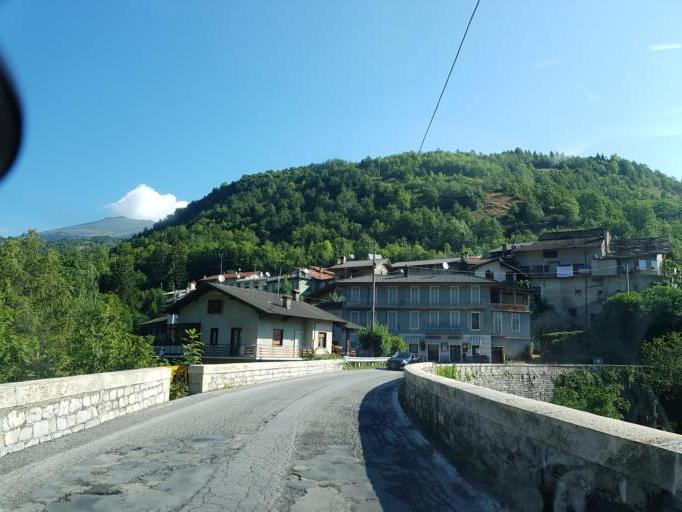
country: IT
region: Piedmont
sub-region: Provincia di Cuneo
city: San Damiano Macra
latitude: 44.4895
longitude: 7.2526
